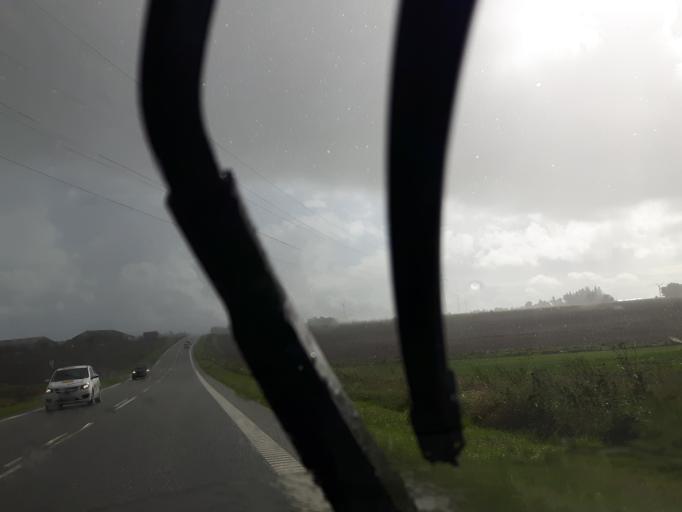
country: DK
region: Central Jutland
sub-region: Struer Kommune
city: Struer
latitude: 56.6233
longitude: 8.5178
